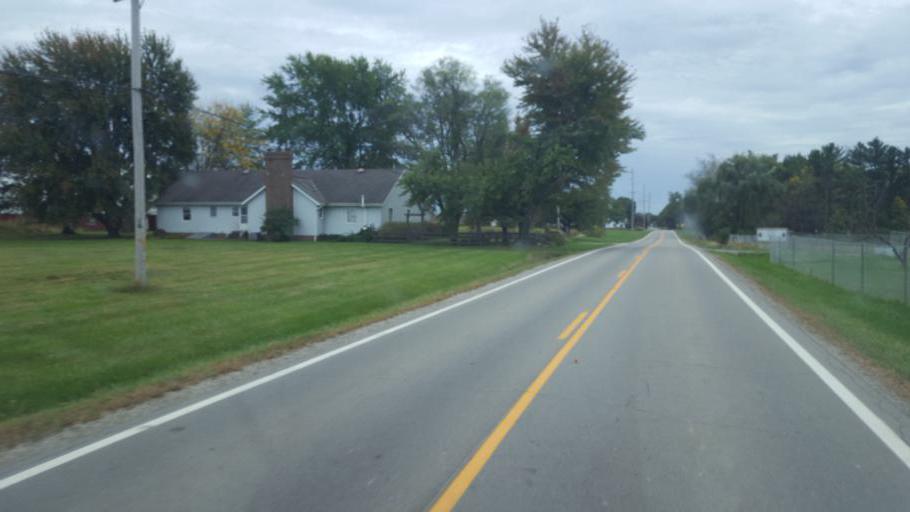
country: US
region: Ohio
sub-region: Huron County
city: Wakeman
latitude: 41.2634
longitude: -82.3965
